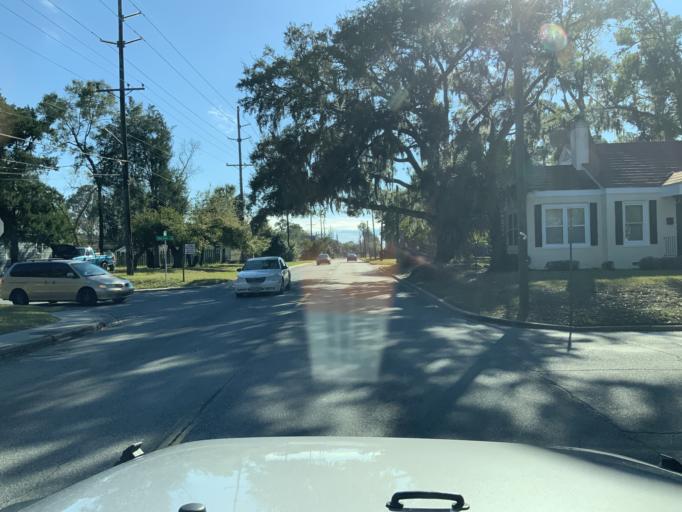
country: US
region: Georgia
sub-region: Chatham County
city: Thunderbolt
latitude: 32.0532
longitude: -81.0633
